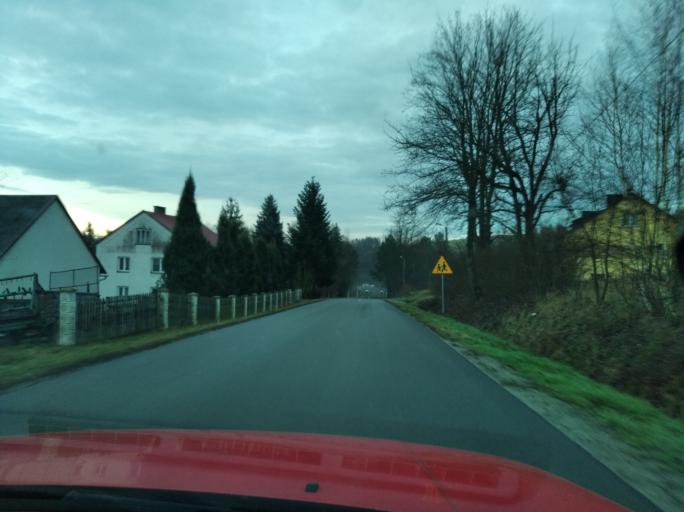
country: PL
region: Subcarpathian Voivodeship
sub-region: Powiat strzyzowski
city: Niebylec
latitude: 49.8695
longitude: 21.8817
